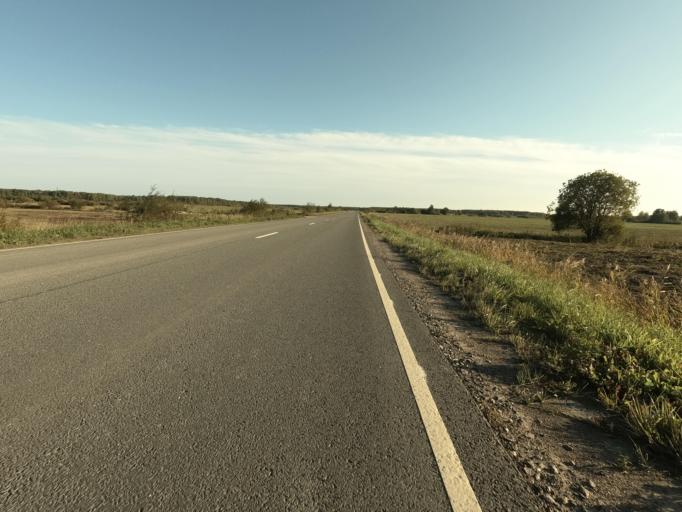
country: RU
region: St.-Petersburg
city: Sapernyy
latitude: 59.7420
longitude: 30.6497
